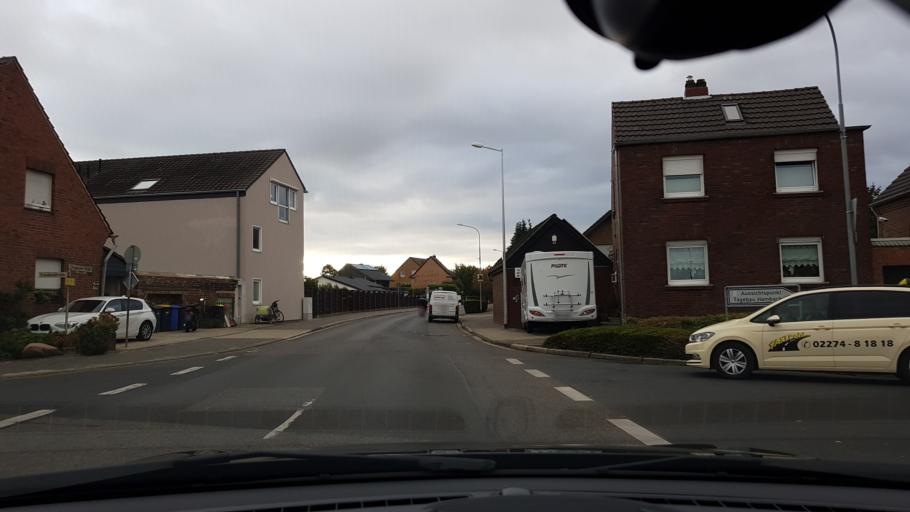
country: DE
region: North Rhine-Westphalia
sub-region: Regierungsbezirk Koln
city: Elsdorf
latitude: 50.9418
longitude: 6.5557
